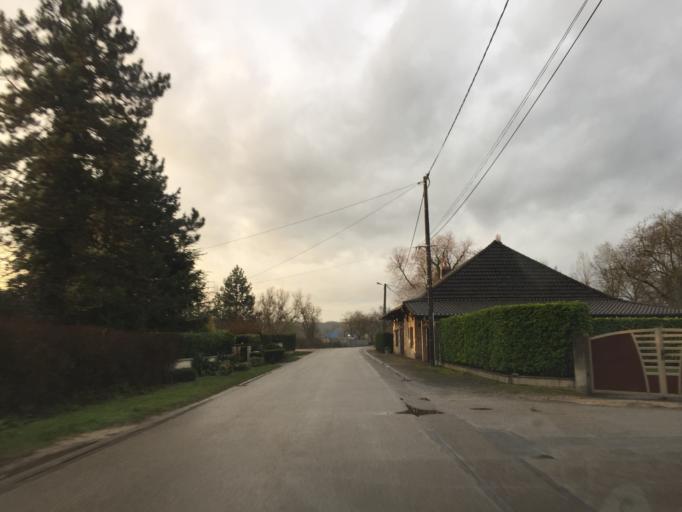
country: FR
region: Franche-Comte
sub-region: Departement du Jura
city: Choisey
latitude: 47.0186
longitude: 5.4831
